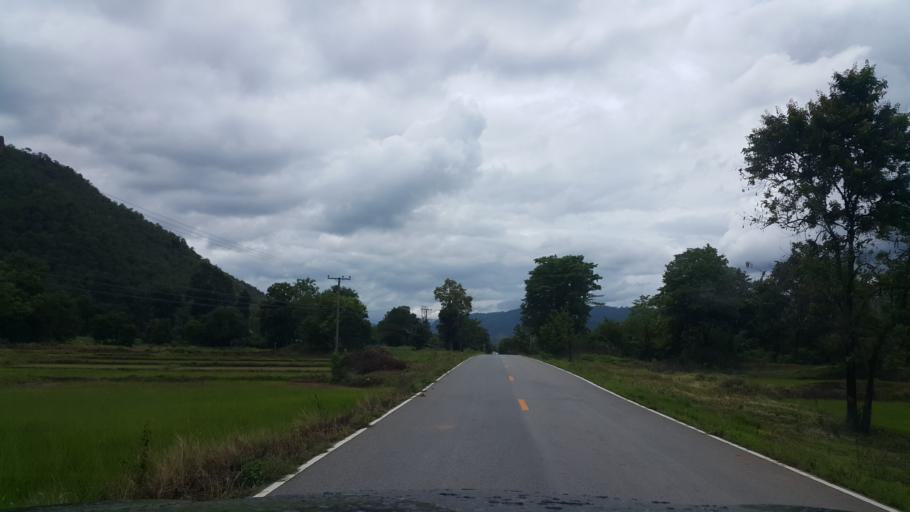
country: TH
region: Phitsanulok
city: Chat Trakan
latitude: 17.3179
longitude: 100.6798
